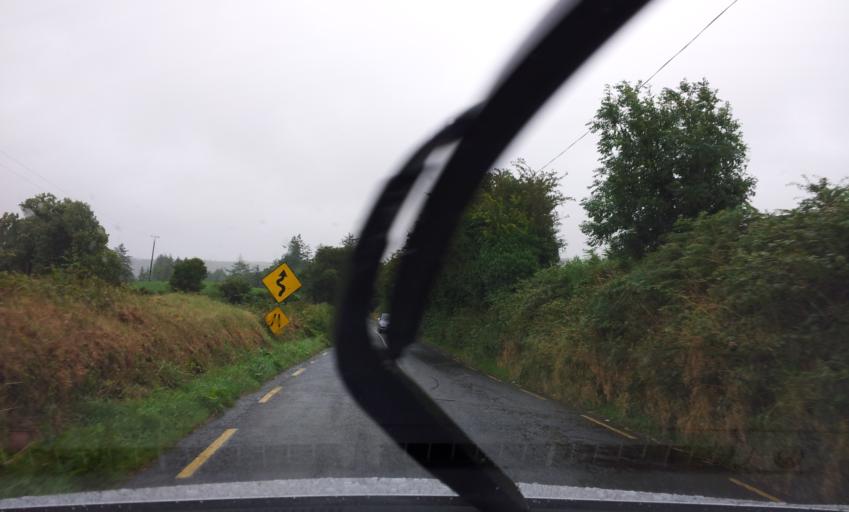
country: IE
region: Leinster
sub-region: Loch Garman
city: New Ross
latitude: 52.4093
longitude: -7.0681
